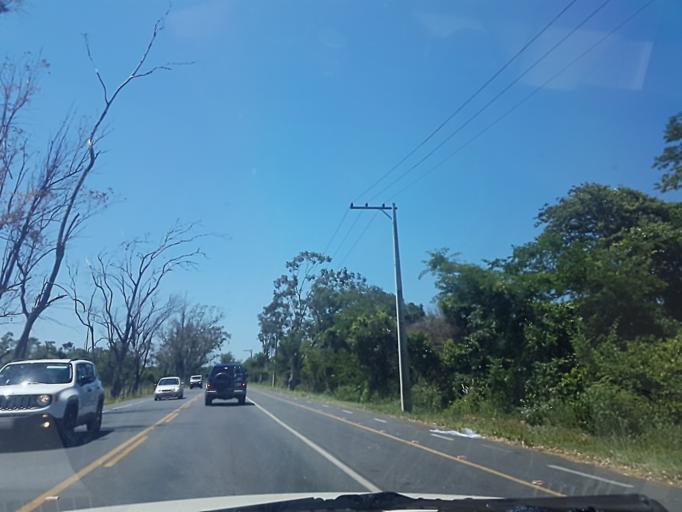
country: PY
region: Cordillera
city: San Bernardino
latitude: -25.2777
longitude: -57.3179
